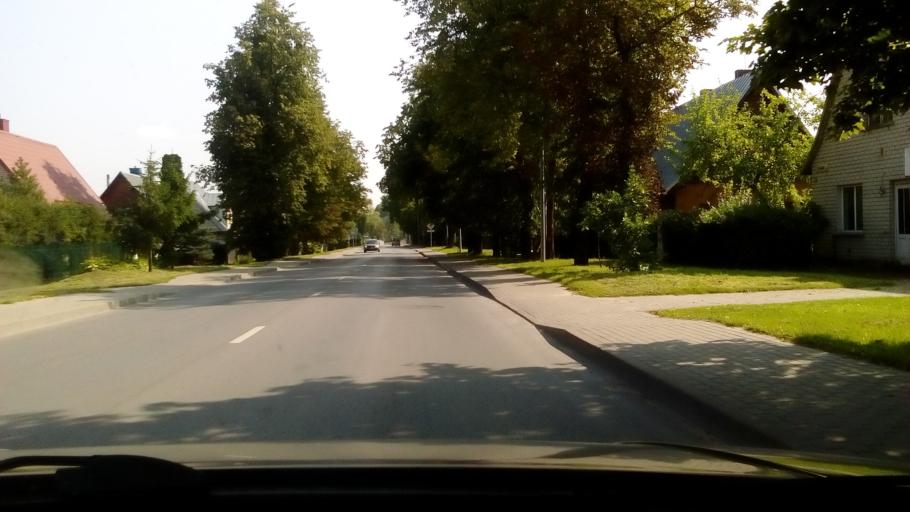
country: LT
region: Alytaus apskritis
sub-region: Alytus
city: Alytus
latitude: 54.4023
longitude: 24.0401
